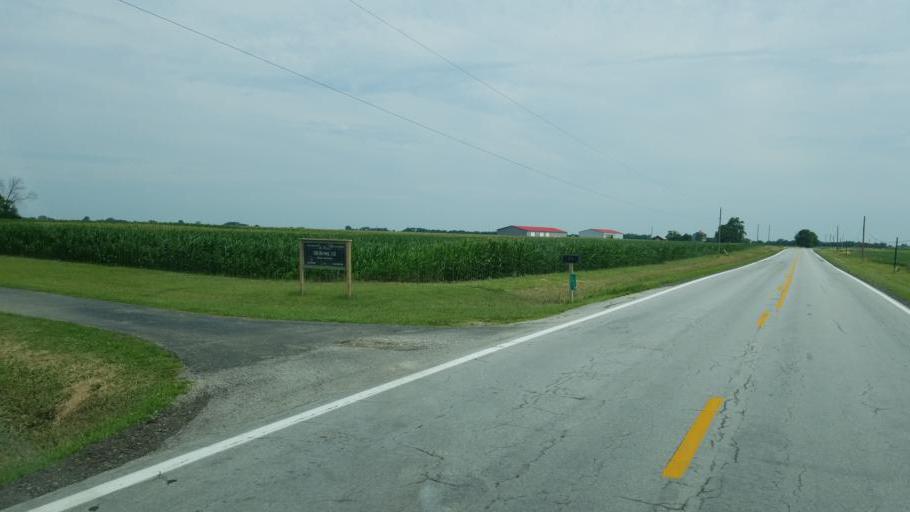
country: US
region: Ohio
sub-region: Madison County
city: Choctaw Lake
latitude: 39.9583
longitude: -83.4337
